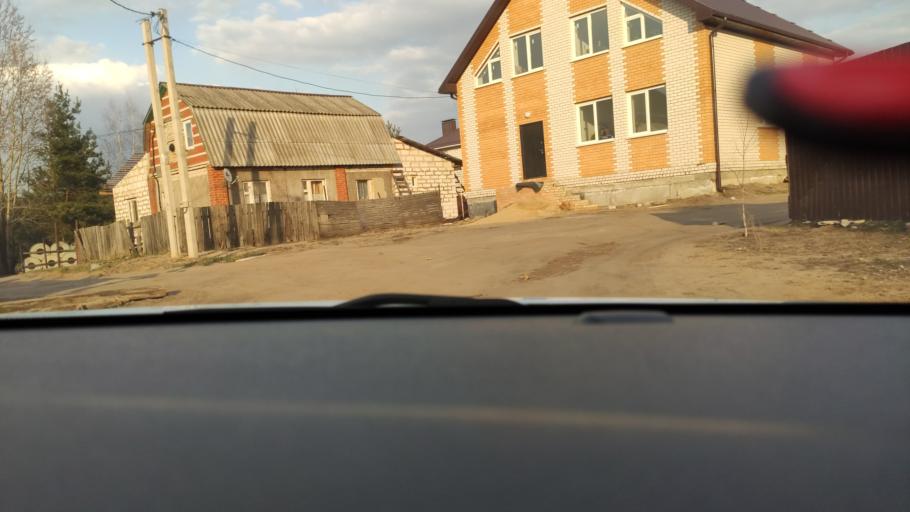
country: RU
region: Voronezj
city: Pridonskoy
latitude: 51.6329
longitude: 39.0956
